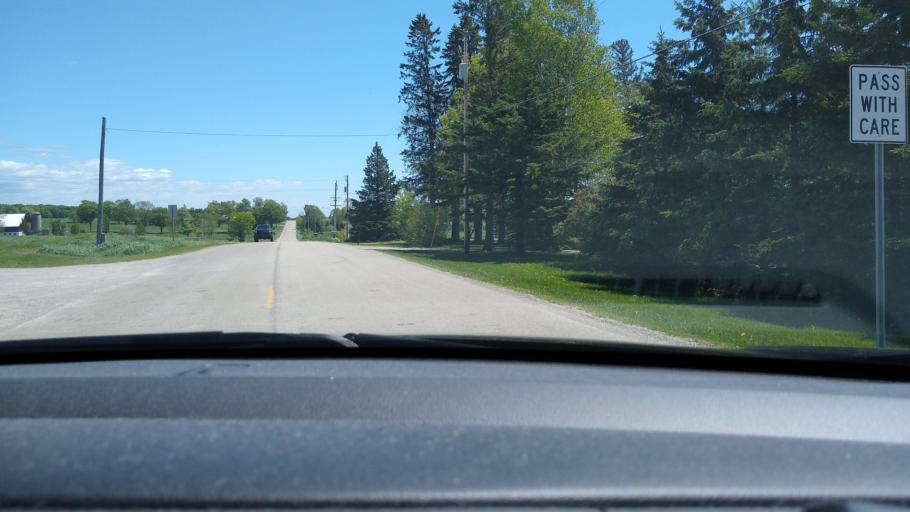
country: US
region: Michigan
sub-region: Delta County
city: Escanaba
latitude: 45.8262
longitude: -87.1436
